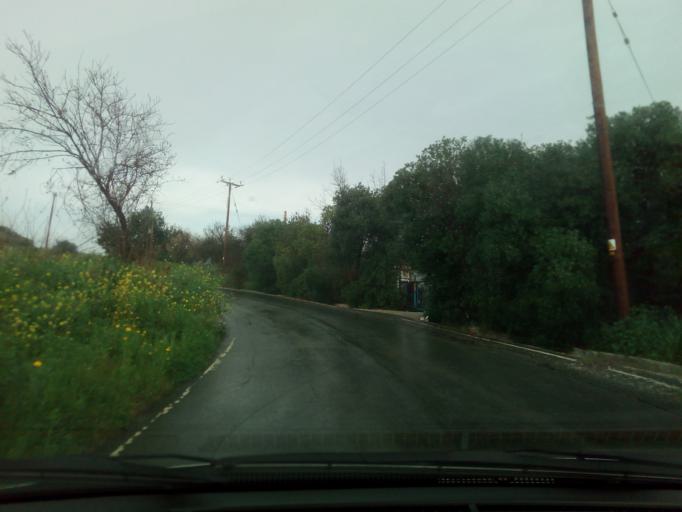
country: CY
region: Pafos
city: Polis
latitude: 34.9793
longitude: 32.4639
